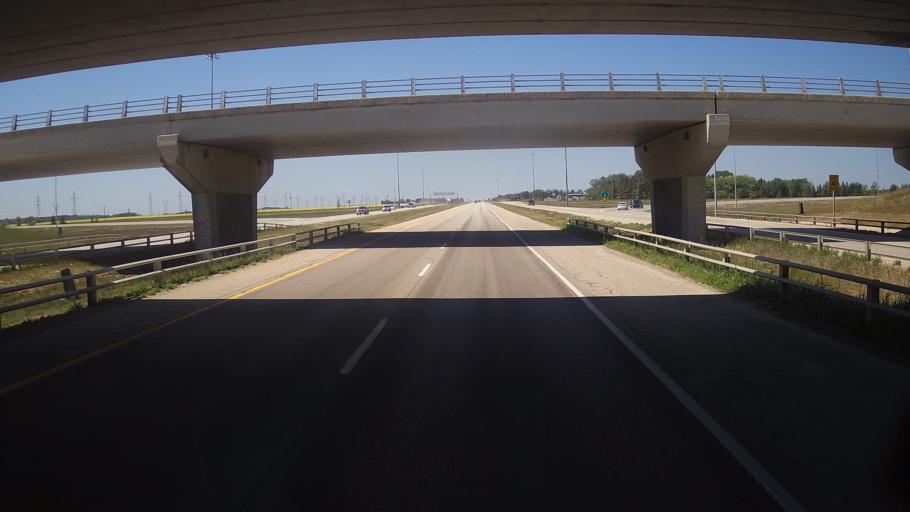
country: CA
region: Manitoba
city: Winnipeg
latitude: 49.9900
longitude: -97.2288
